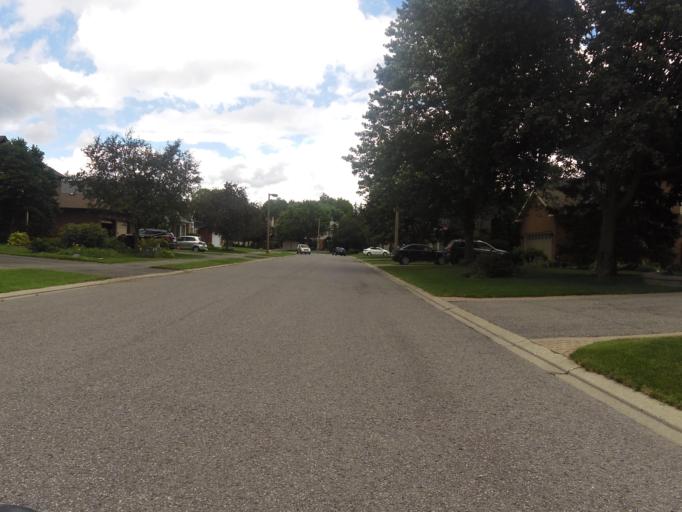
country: CA
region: Ontario
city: Bells Corners
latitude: 45.3192
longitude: -75.9125
